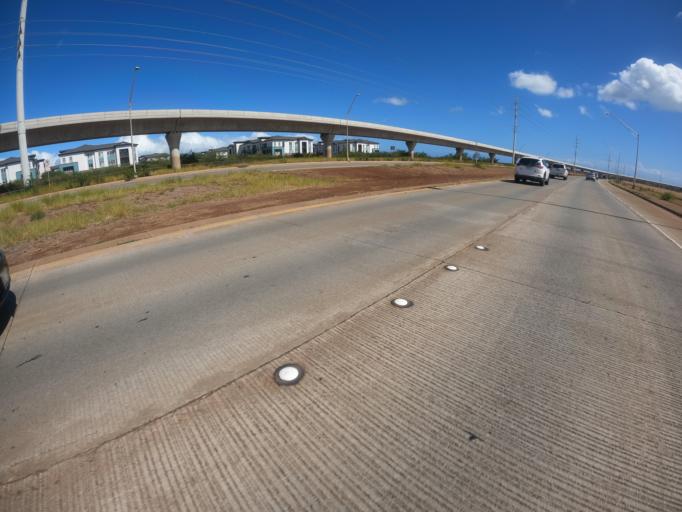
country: US
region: Hawaii
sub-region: Honolulu County
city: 'Ewa Villages
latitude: 21.3566
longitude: -158.0507
